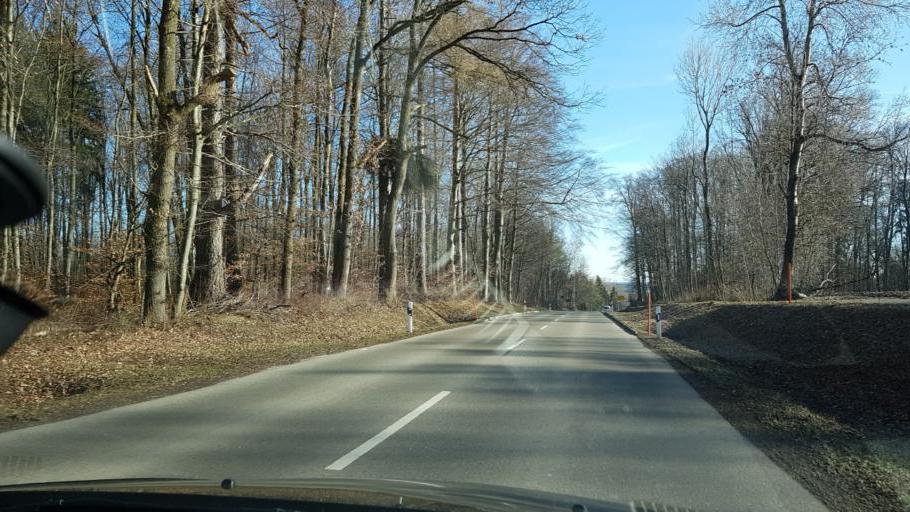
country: DE
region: Bavaria
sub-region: Upper Bavaria
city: Oberschweinbach
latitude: 48.2221
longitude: 11.1777
